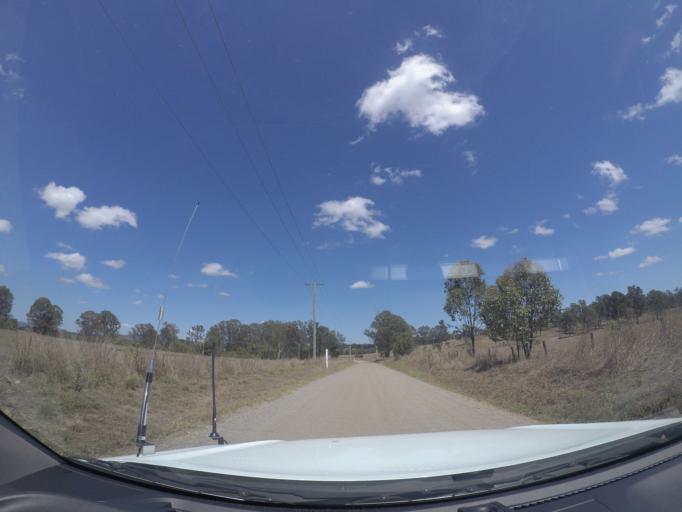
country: AU
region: Queensland
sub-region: Logan
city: Cedar Vale
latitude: -27.8390
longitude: 152.9205
